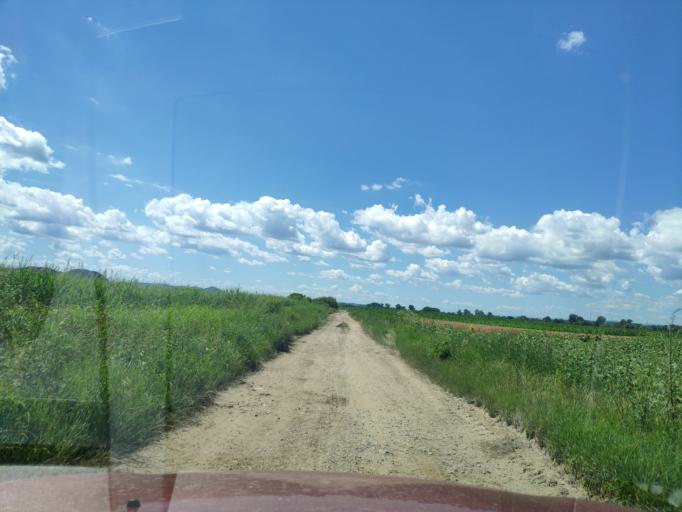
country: HU
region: Borsod-Abauj-Zemplen
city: Ozd
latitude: 48.2857
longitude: 20.2029
